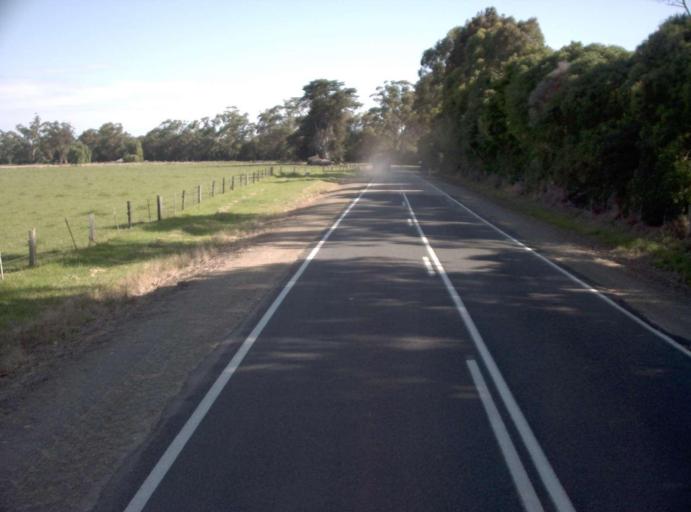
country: AU
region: Victoria
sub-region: East Gippsland
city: Lakes Entrance
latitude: -37.7344
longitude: 148.5050
